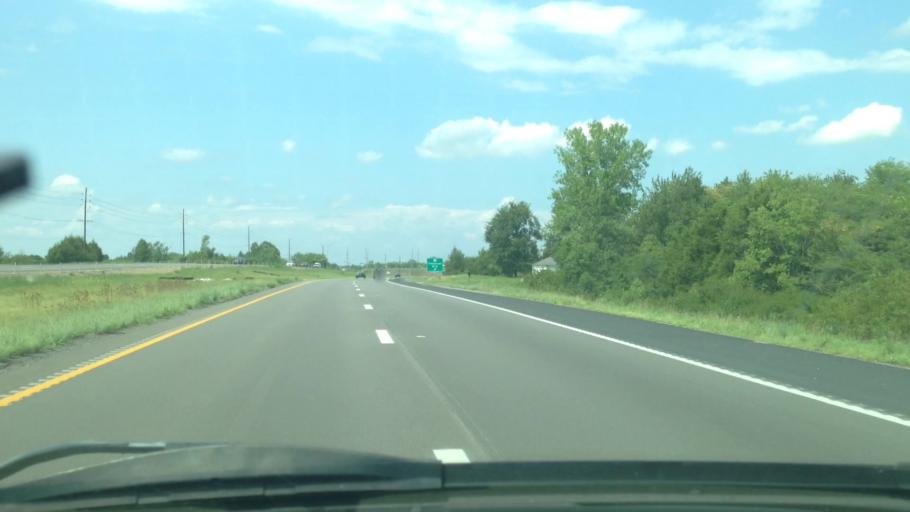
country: US
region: Missouri
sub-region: Lincoln County
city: Moscow Mills
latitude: 38.9007
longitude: -90.9218
